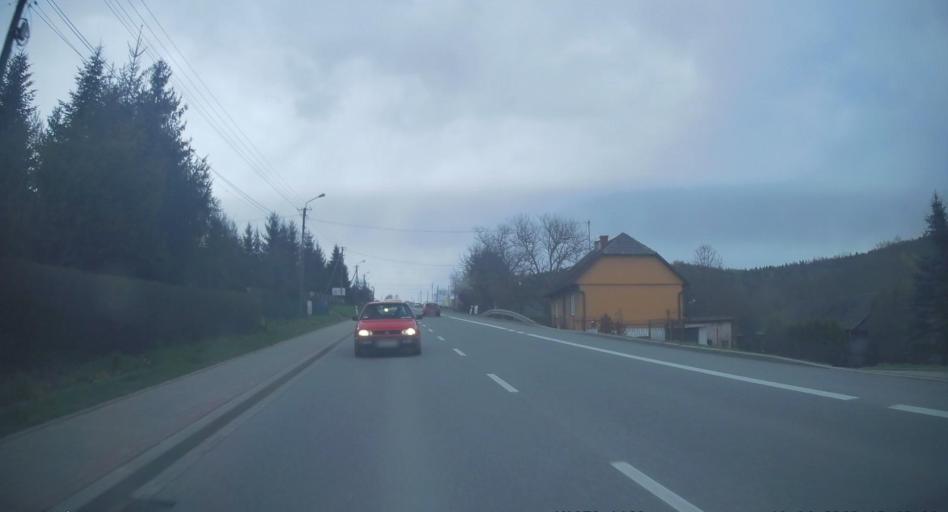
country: PL
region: Lesser Poland Voivodeship
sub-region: Powiat bochenski
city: Lapczyca
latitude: 49.9599
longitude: 20.3899
